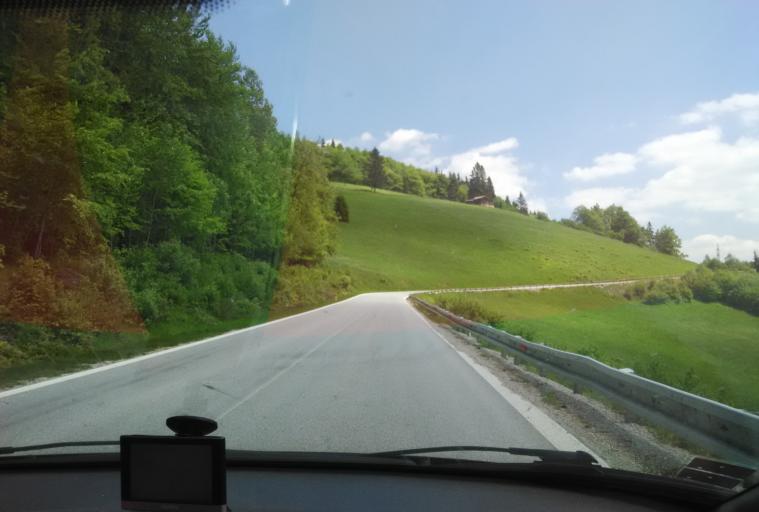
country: SK
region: Kosicky
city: Dobsina
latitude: 48.8470
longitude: 20.3742
